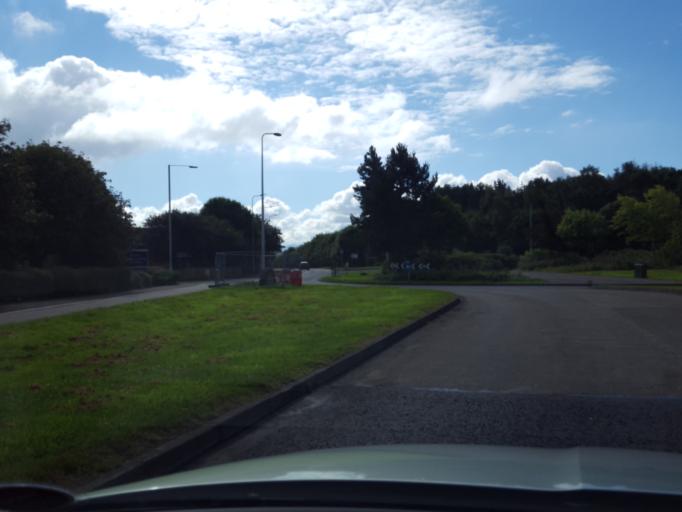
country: GB
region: Scotland
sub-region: Fife
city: Dunfermline
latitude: 56.0587
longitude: -3.4421
